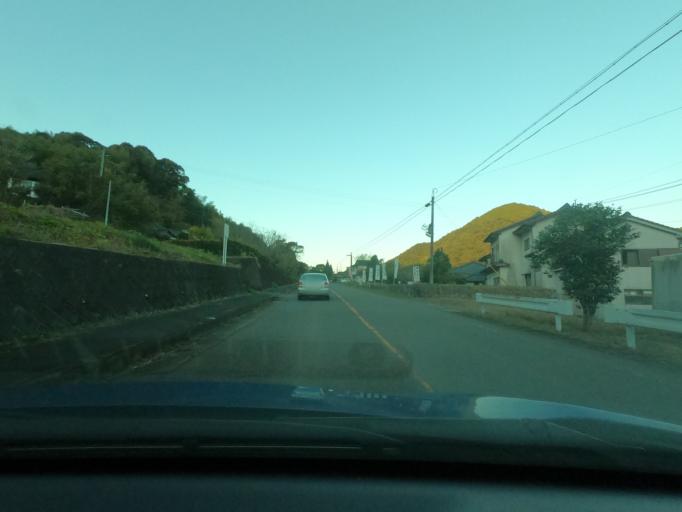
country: JP
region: Kagoshima
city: Satsumasendai
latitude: 31.8003
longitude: 130.4795
